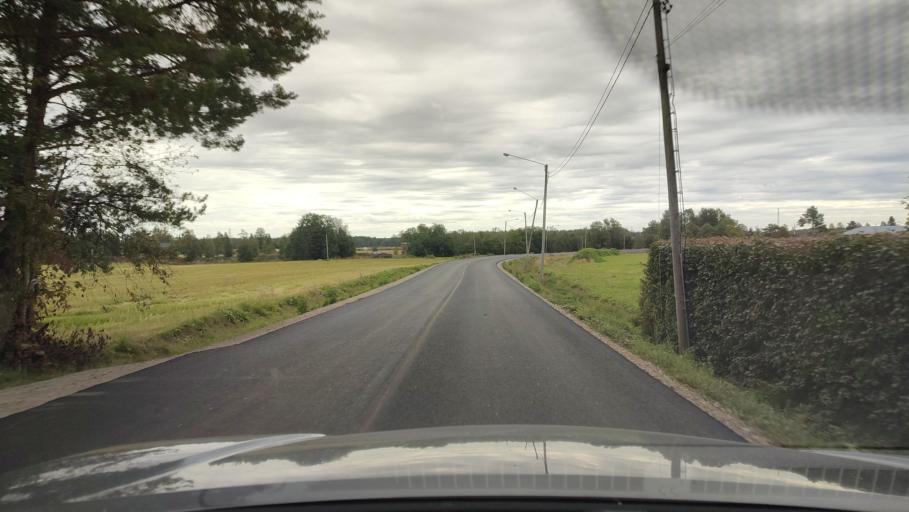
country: FI
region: Southern Ostrobothnia
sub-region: Suupohja
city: Karijoki
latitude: 62.2494
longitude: 21.5503
